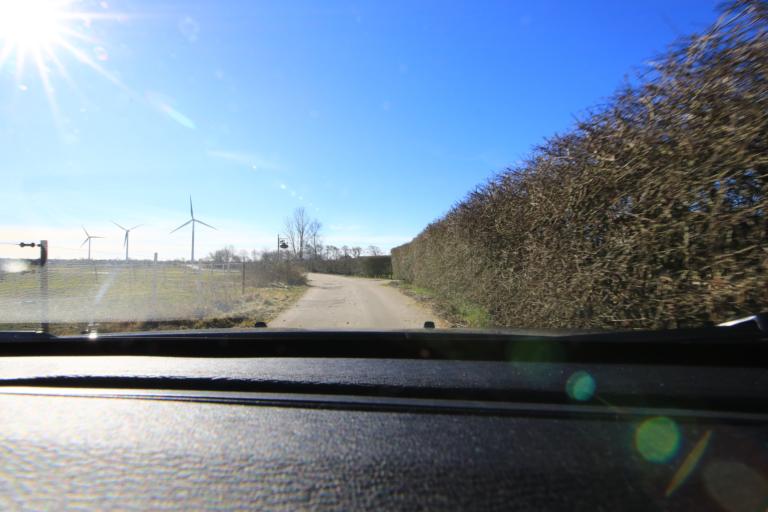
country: SE
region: Halland
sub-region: Varbergs Kommun
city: Tvaaker
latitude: 57.0469
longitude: 12.3743
